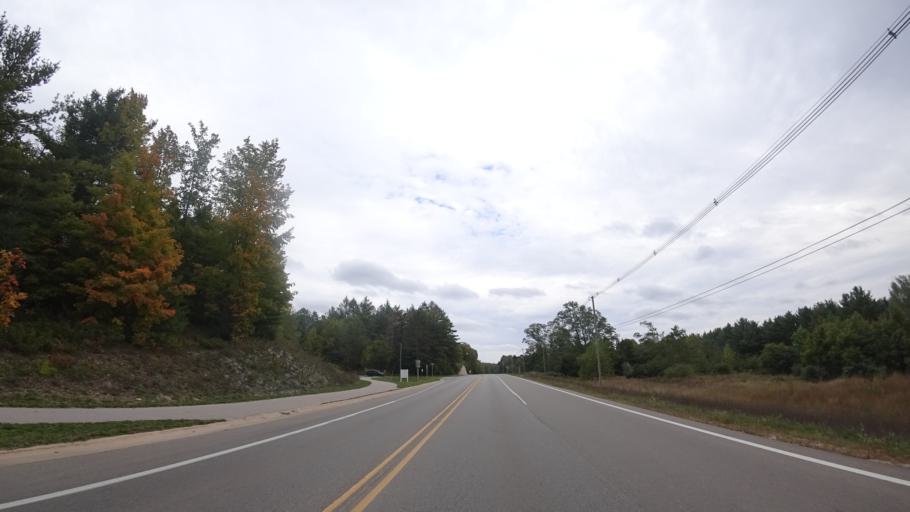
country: US
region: Michigan
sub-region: Emmet County
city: Harbor Springs
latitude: 45.4315
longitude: -84.9447
